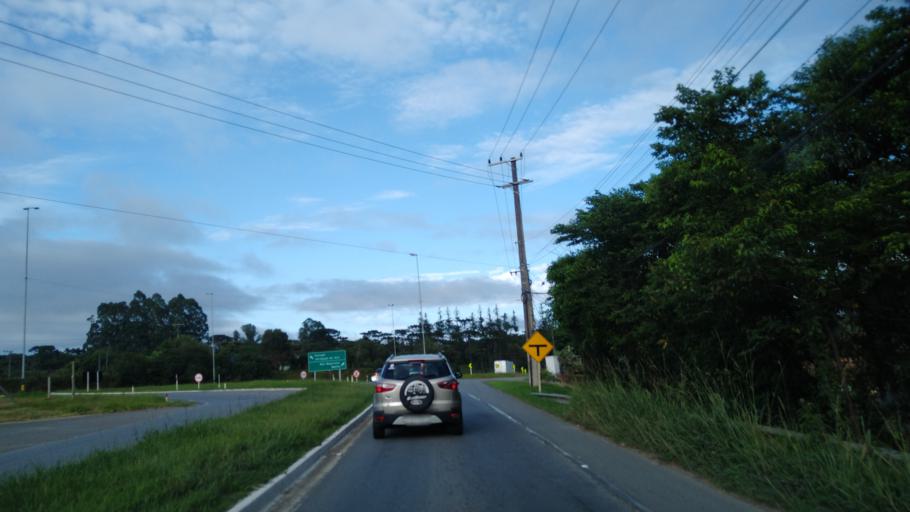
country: BR
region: Santa Catarina
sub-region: Rio Negrinho
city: Rio Negrinho
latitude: -26.2449
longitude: -49.4599
